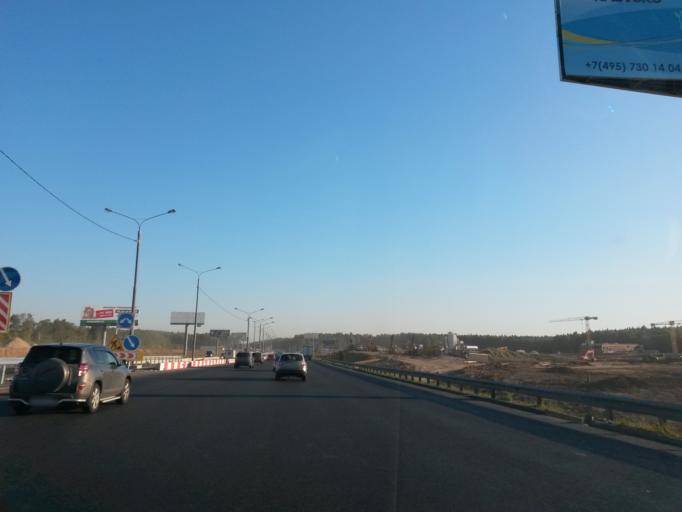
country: RU
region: Moskovskaya
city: Shcherbinka
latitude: 55.5266
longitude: 37.6100
